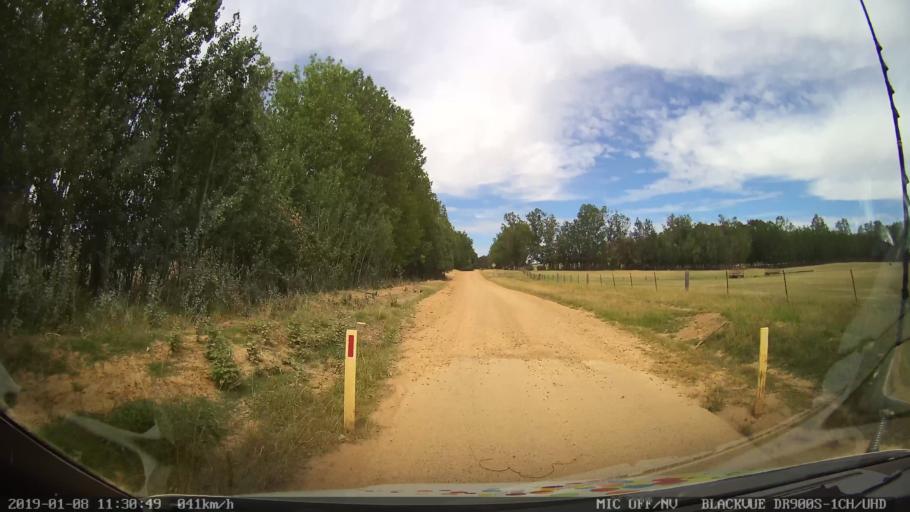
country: AU
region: New South Wales
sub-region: Guyra
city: Guyra
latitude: -30.3097
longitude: 151.5421
